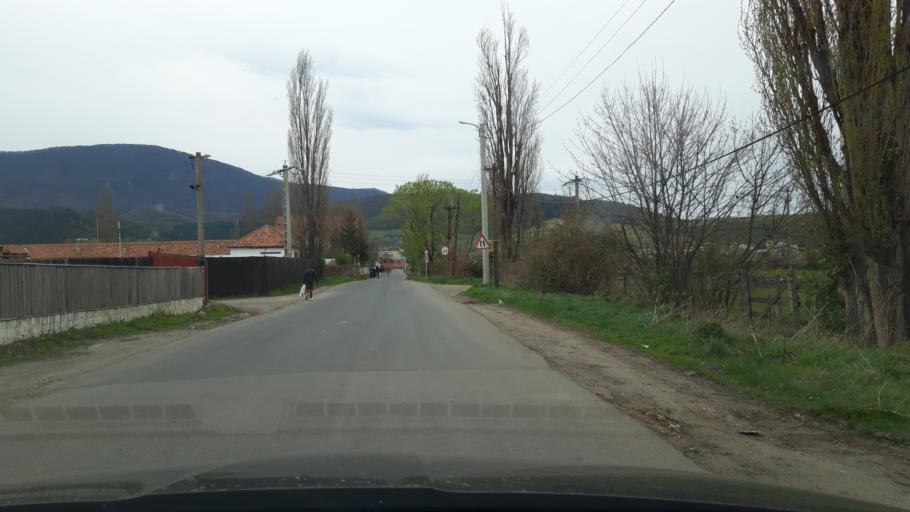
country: RO
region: Brasov
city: Codlea
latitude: 45.6997
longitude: 25.4597
